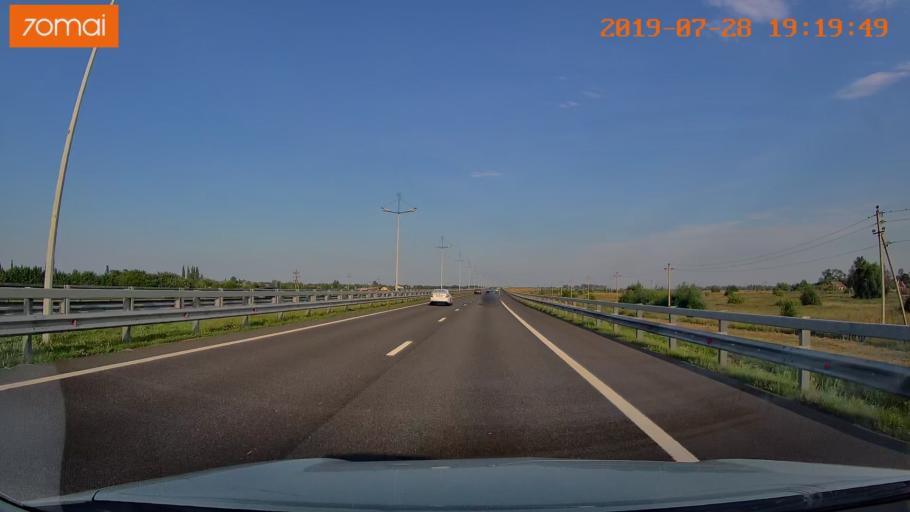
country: RU
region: Kaliningrad
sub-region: Zelenogradskiy Rayon
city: Zelenogradsk
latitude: 54.9192
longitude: 20.4697
